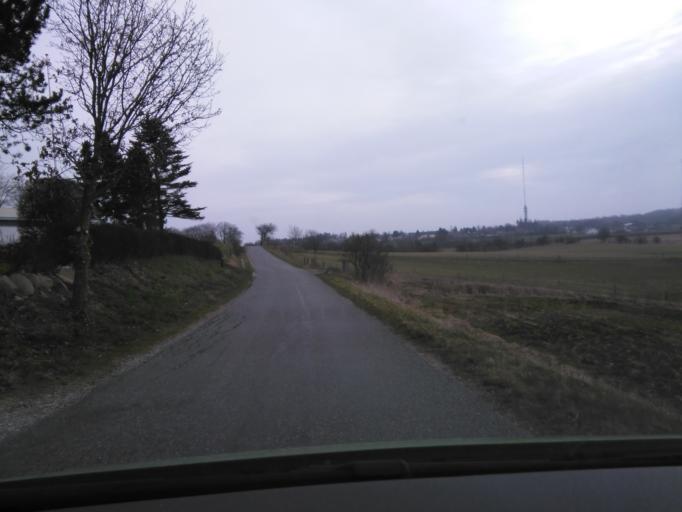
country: DK
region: Central Jutland
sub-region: Arhus Kommune
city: Marslet
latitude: 56.0986
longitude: 10.1884
